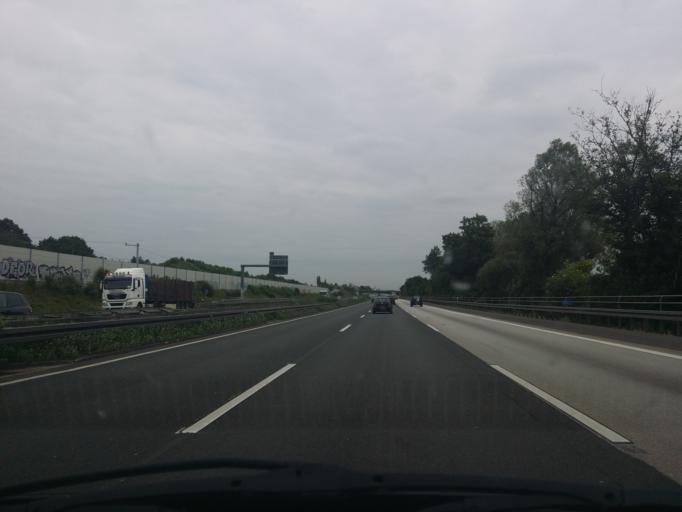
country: DE
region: Hesse
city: Eppstein
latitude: 50.0850
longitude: 8.3592
